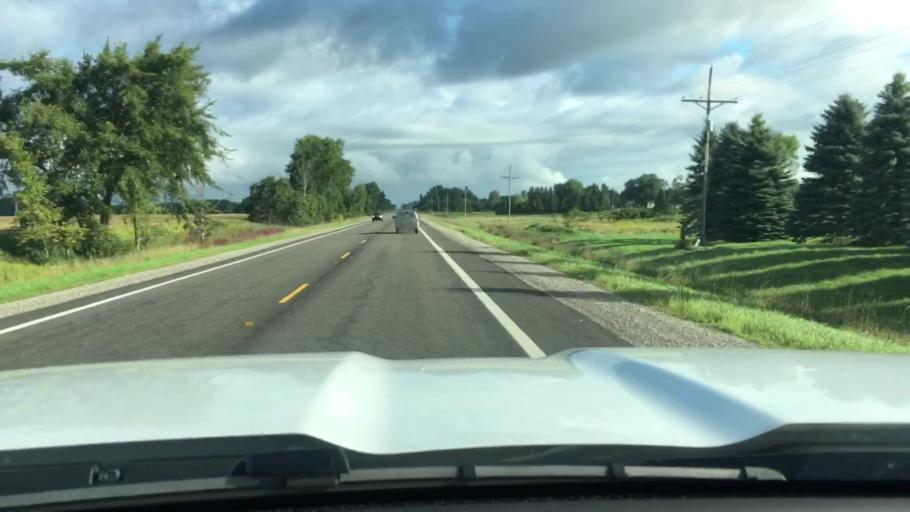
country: US
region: Michigan
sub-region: Tuscola County
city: Caro
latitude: 43.3897
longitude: -83.3834
